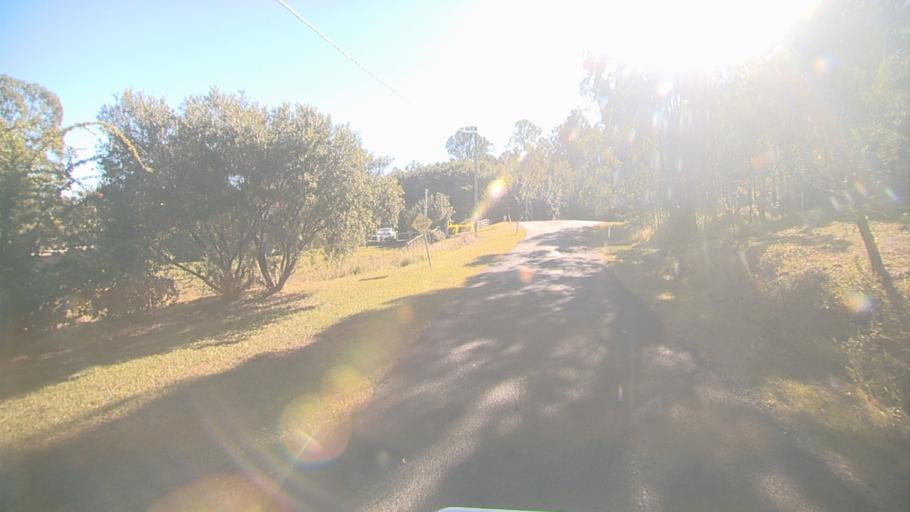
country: AU
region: Queensland
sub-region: Logan
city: Windaroo
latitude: -27.7788
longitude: 153.1479
